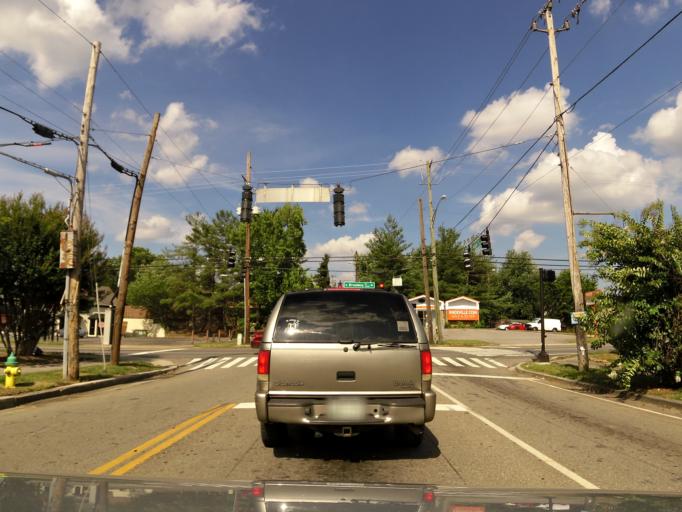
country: US
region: Tennessee
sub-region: Knox County
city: Knoxville
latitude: 36.0000
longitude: -83.9257
